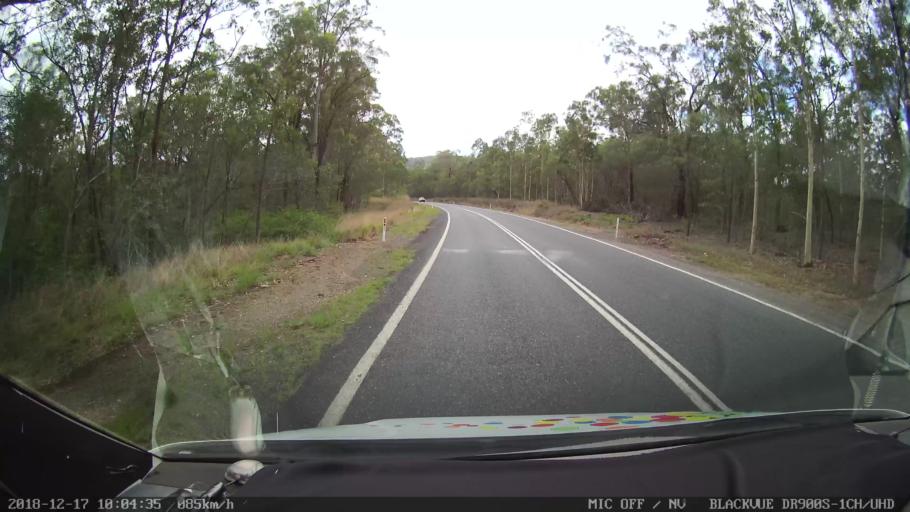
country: AU
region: New South Wales
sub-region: Tenterfield Municipality
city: Carrolls Creek
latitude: -28.8953
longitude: 152.4790
